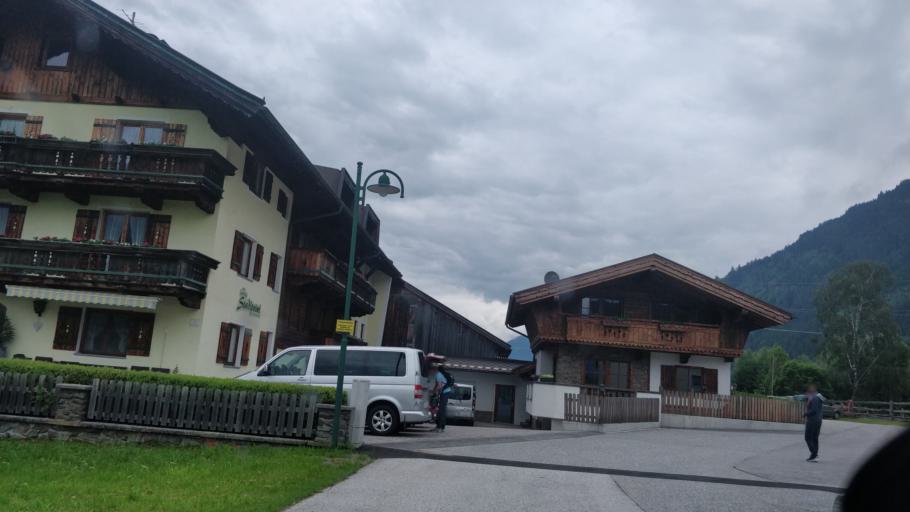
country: AT
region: Tyrol
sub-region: Politischer Bezirk Schwaz
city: Ried im Zillertal
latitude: 47.3060
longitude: 11.8730
